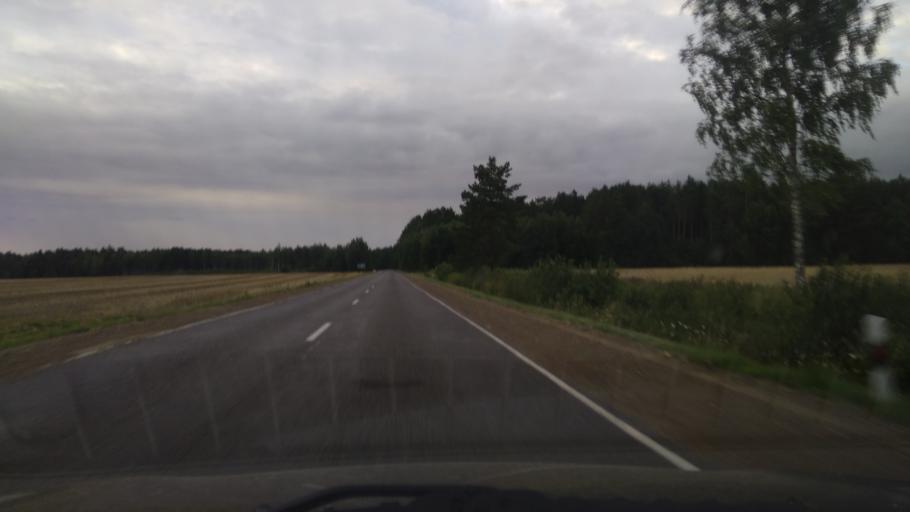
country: BY
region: Brest
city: Byaroza
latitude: 52.4012
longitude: 25.0031
